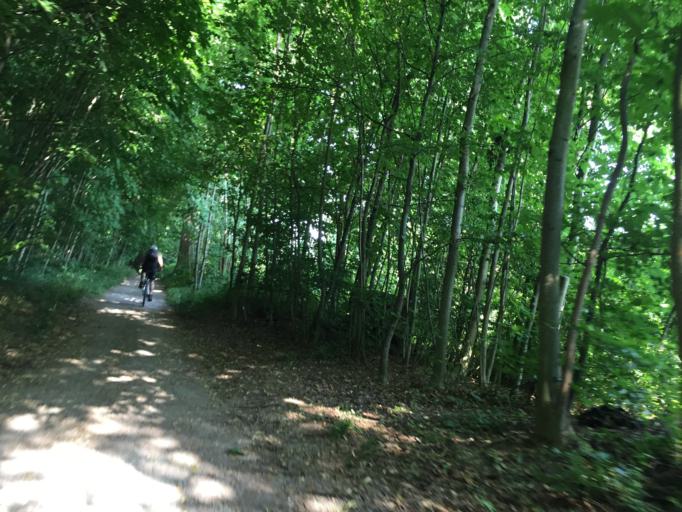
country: CH
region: Bern
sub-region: Bern-Mittelland District
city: Bolligen
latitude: 46.9676
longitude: 7.4742
